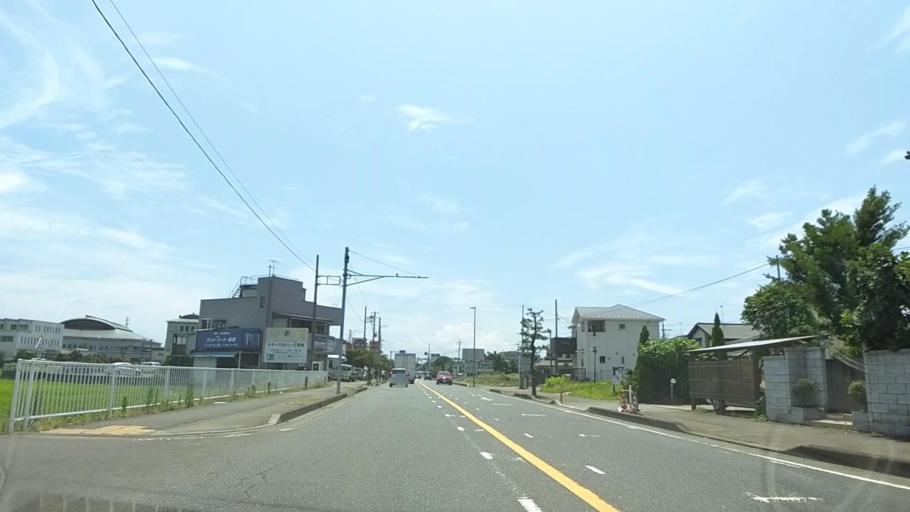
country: JP
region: Kanagawa
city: Chigasaki
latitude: 35.3783
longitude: 139.3853
